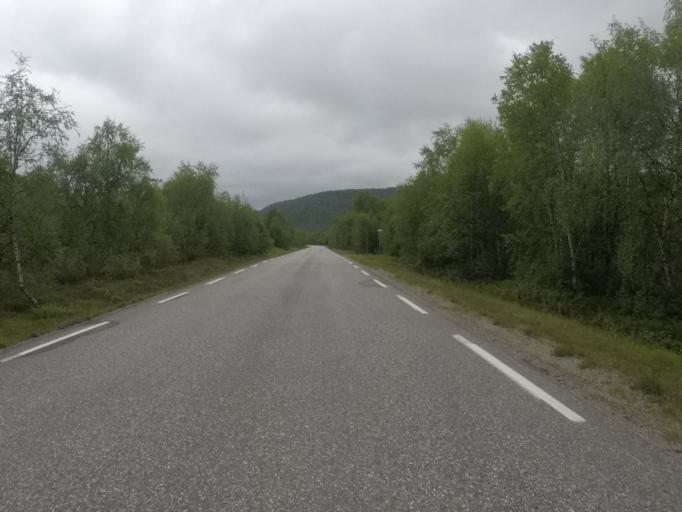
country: NO
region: Finnmark Fylke
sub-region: Karasjok
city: Karasjohka
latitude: 69.6436
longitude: 25.9508
